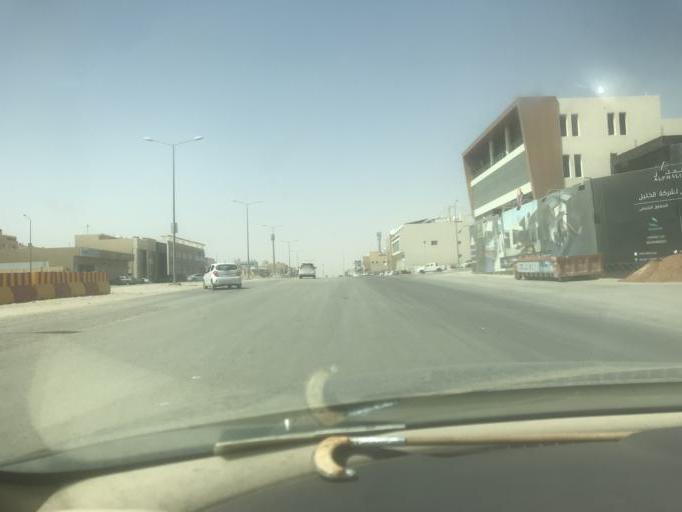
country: SA
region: Ar Riyad
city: Riyadh
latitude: 24.8168
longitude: 46.5974
